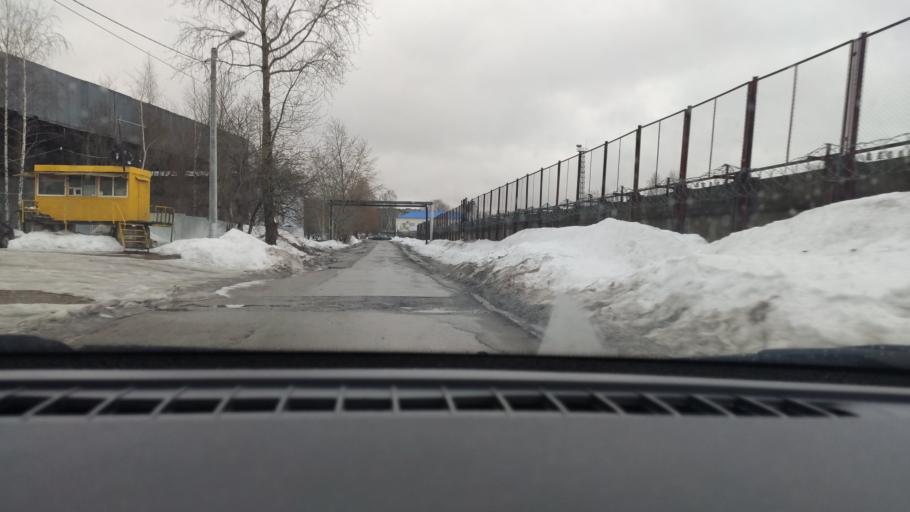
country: RU
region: Perm
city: Perm
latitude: 58.1066
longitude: 56.3774
